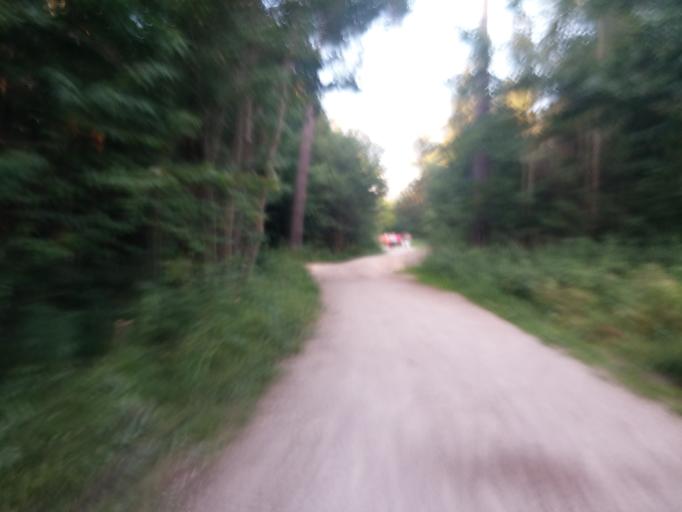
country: DE
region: Bavaria
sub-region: Upper Bavaria
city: Putzbrunn
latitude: 48.0973
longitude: 11.6940
